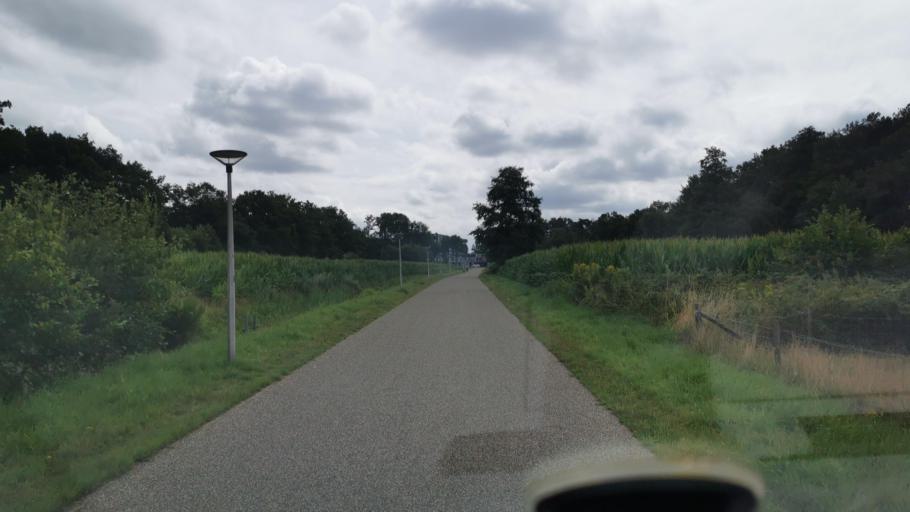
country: NL
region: Overijssel
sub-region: Gemeente Enschede
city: Enschede
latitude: 52.2197
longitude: 6.9510
